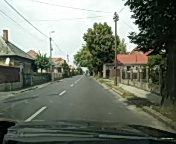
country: HU
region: Hajdu-Bihar
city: Debrecen
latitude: 47.5313
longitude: 21.6605
